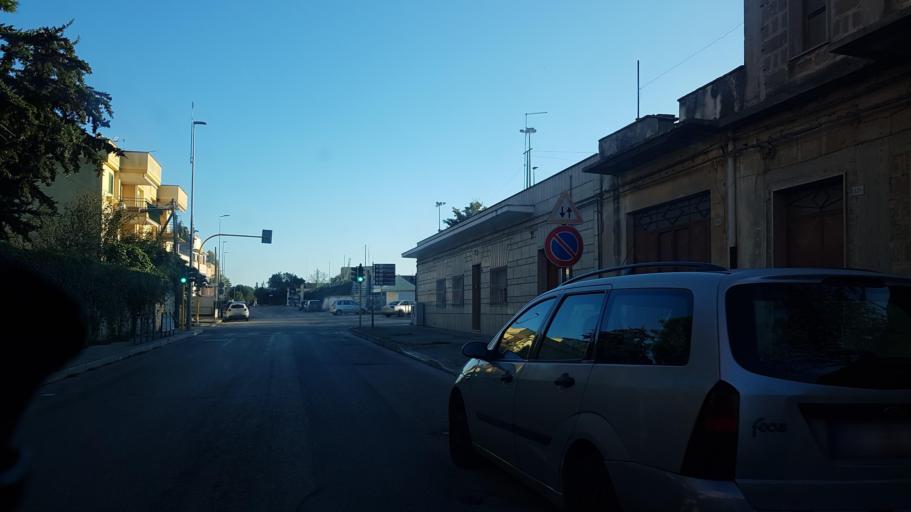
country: IT
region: Apulia
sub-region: Provincia di Brindisi
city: Latiano
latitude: 40.5482
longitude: 17.7193
